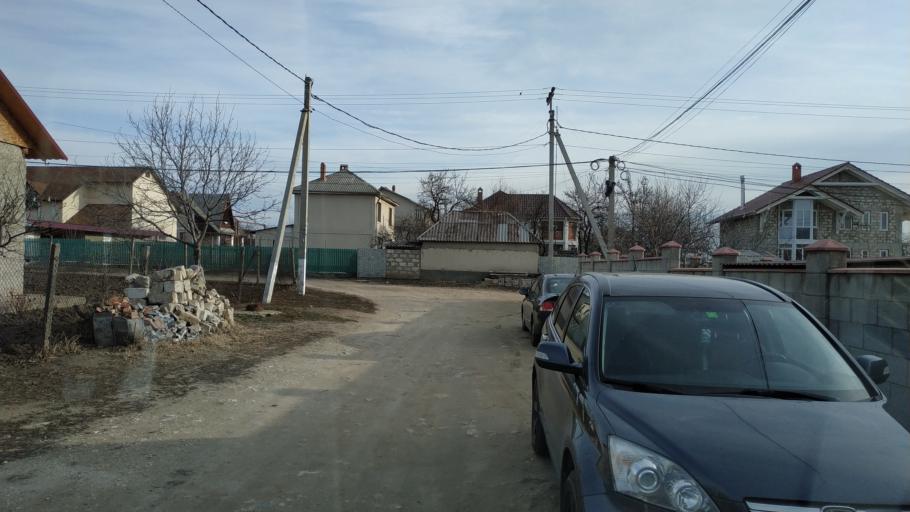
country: MD
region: Chisinau
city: Vatra
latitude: 46.9846
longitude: 28.6785
